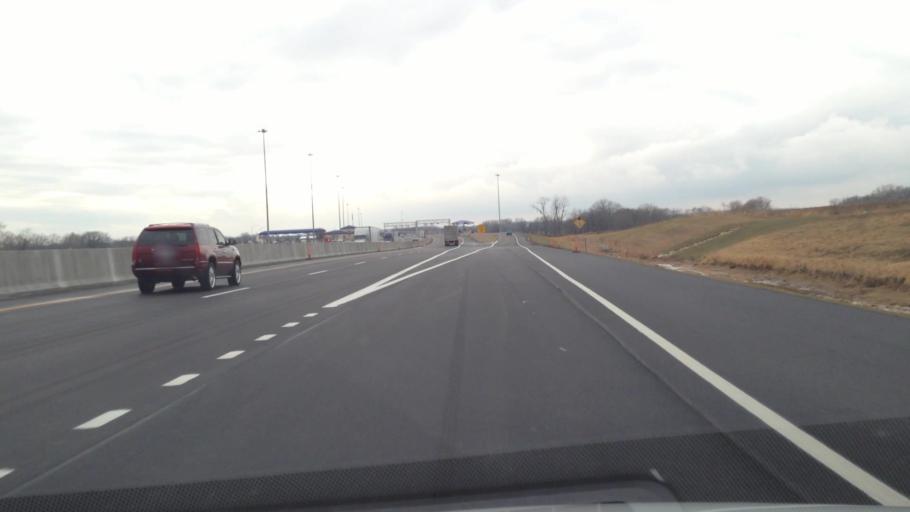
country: US
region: Kansas
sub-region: Leavenworth County
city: Basehor
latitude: 39.0717
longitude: -95.0016
